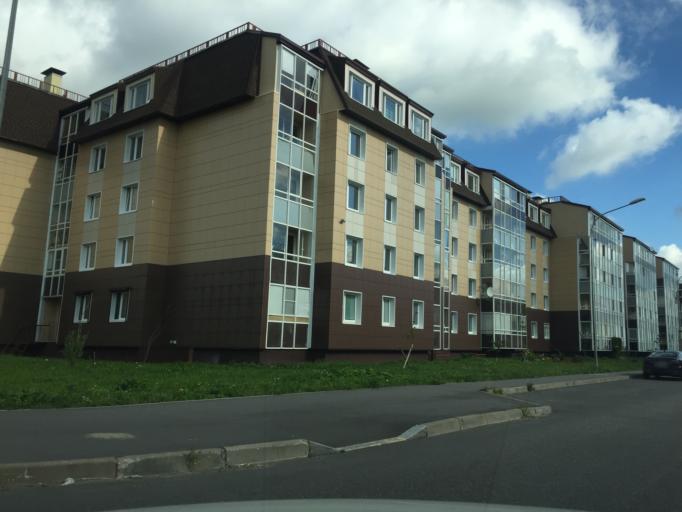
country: RU
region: St.-Petersburg
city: Aleksandrovskaya
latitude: 59.7542
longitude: 30.3724
